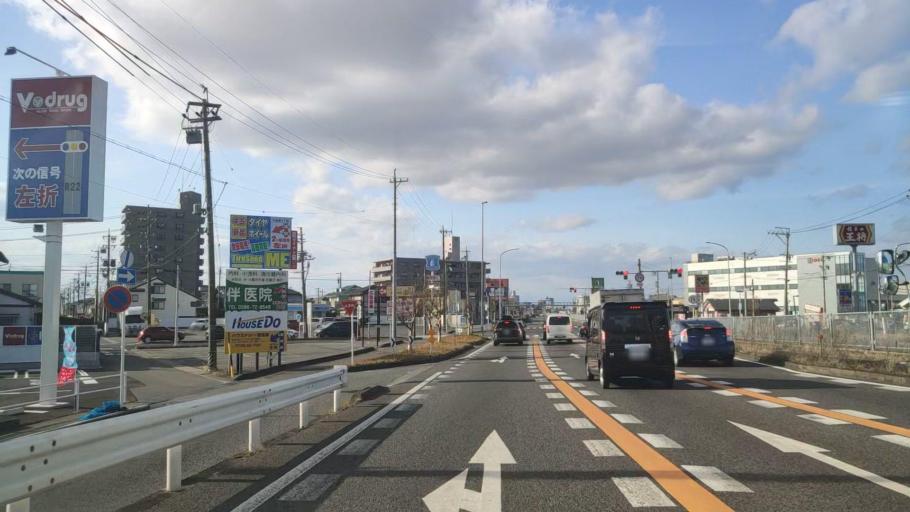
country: JP
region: Aichi
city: Ichinomiya
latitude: 35.3168
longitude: 136.8136
